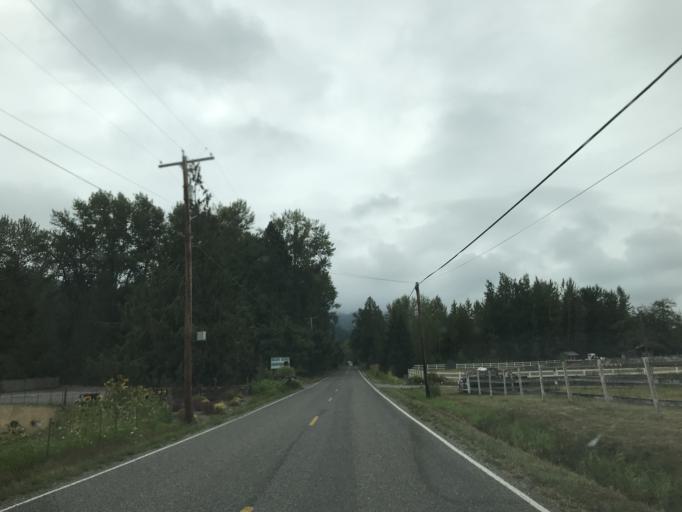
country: US
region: Washington
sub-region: Whatcom County
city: Sudden Valley
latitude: 48.8014
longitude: -122.3362
